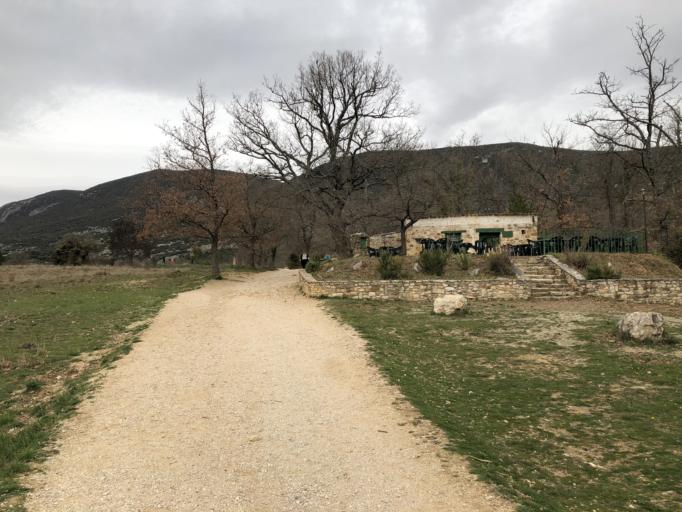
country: FR
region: Provence-Alpes-Cote d'Azur
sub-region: Departement du Vaucluse
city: Saignon
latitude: 43.9163
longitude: 5.4970
